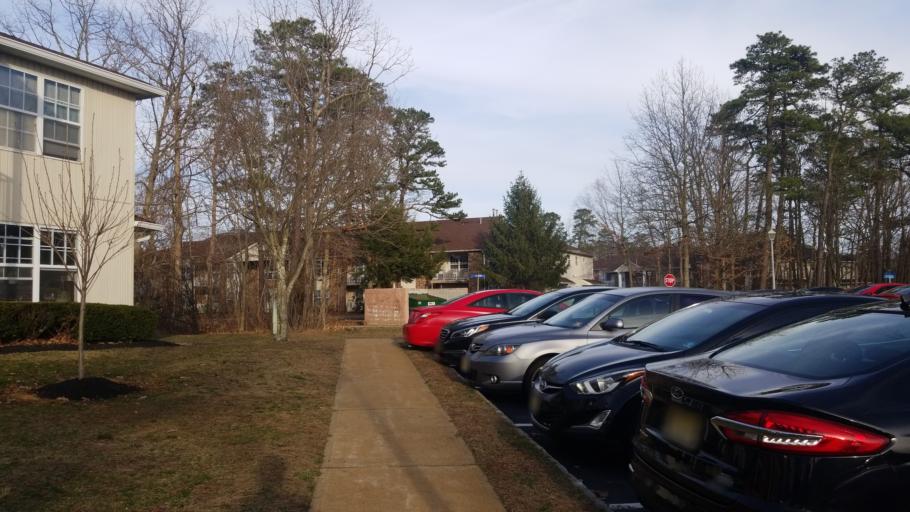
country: US
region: New Jersey
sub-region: Ocean County
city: Leisure Knoll
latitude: 39.9994
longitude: -74.2920
